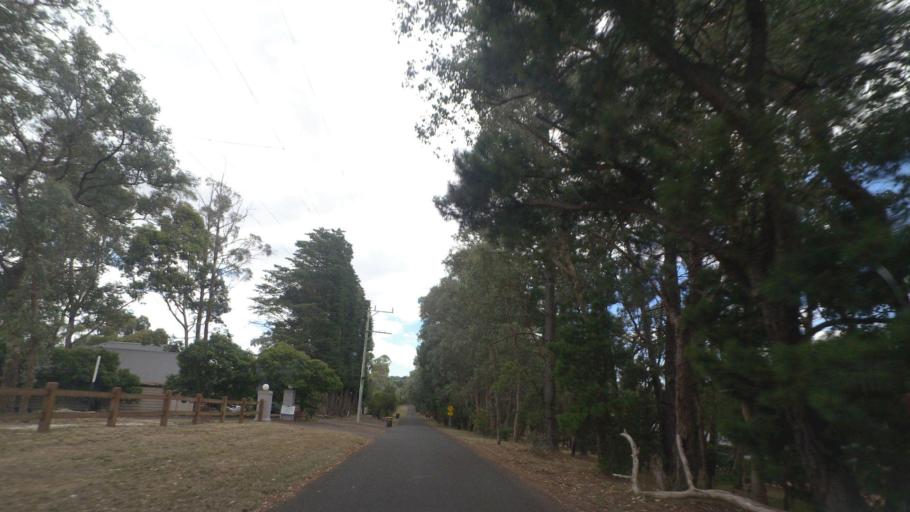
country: AU
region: Victoria
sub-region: Manningham
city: Warrandyte
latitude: -37.7520
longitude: 145.2507
